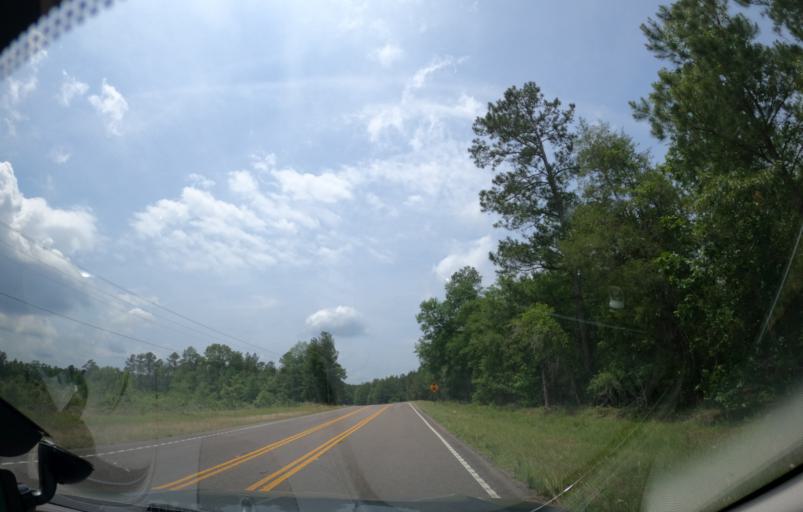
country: US
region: South Carolina
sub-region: Barnwell County
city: Williston
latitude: 33.5735
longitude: -81.4653
